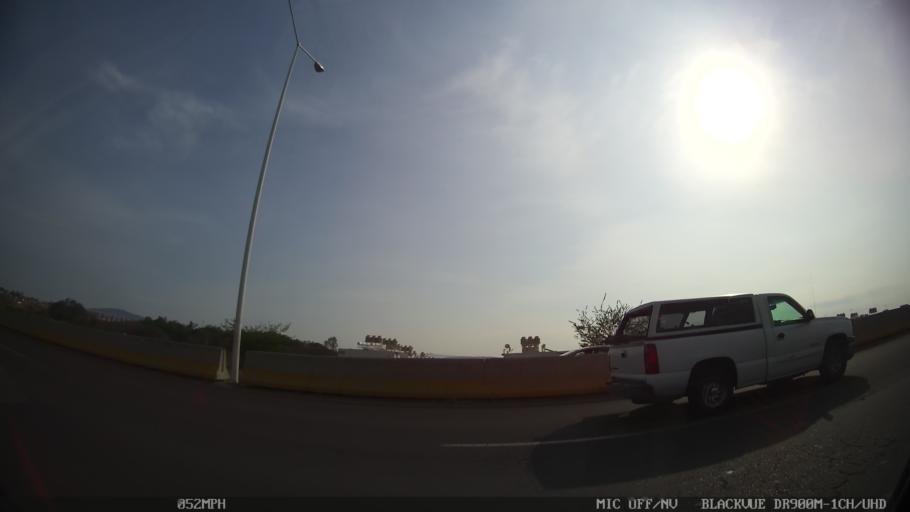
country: MX
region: Jalisco
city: Coyula
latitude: 20.6551
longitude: -103.2110
